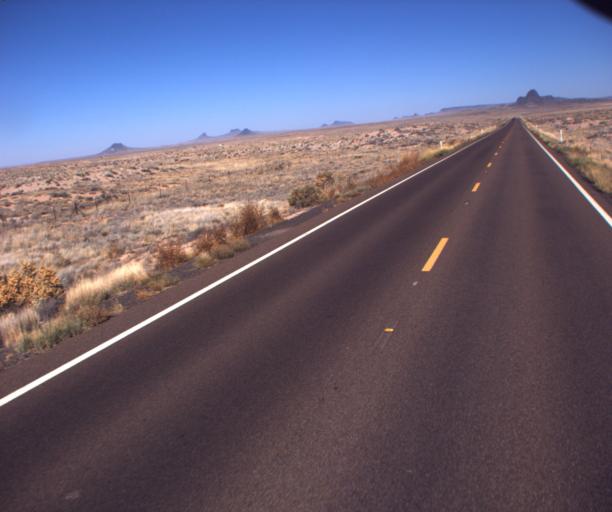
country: US
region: Arizona
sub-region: Navajo County
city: Dilkon
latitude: 35.2195
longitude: -110.4359
